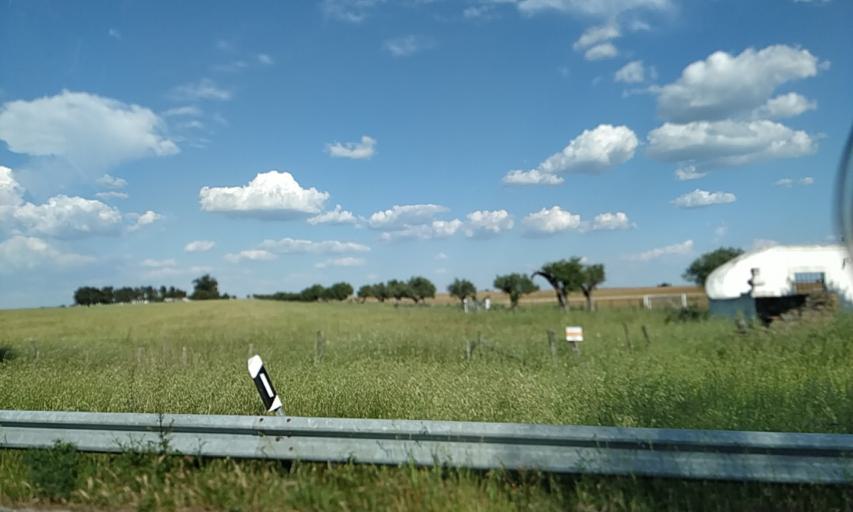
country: PT
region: Evora
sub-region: Estremoz
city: Estremoz
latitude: 38.9828
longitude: -7.4823
